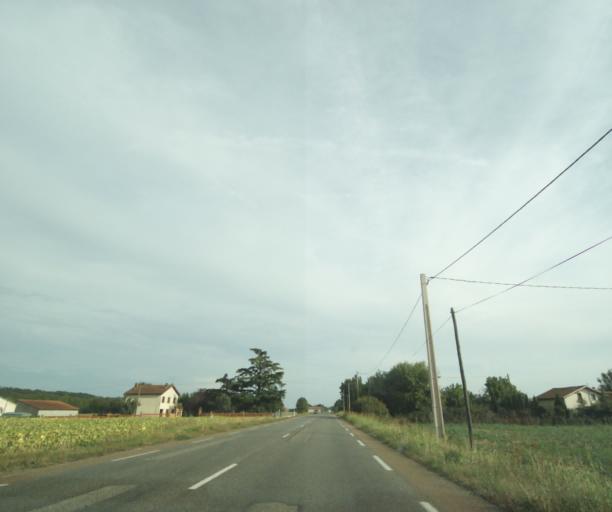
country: FR
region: Midi-Pyrenees
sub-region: Departement du Tarn-et-Garonne
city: Verdun-sur-Garonne
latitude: 43.8722
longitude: 1.2627
